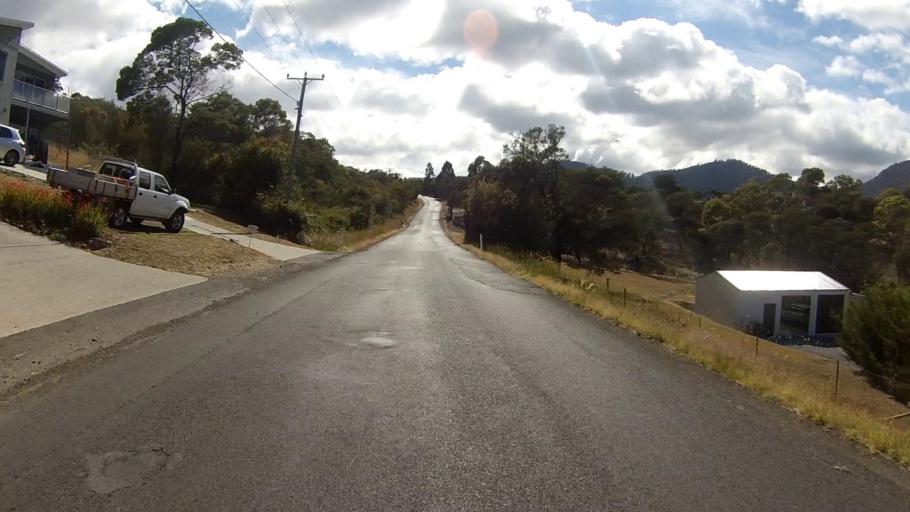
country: AU
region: Tasmania
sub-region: Brighton
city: Old Beach
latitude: -42.7760
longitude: 147.2840
